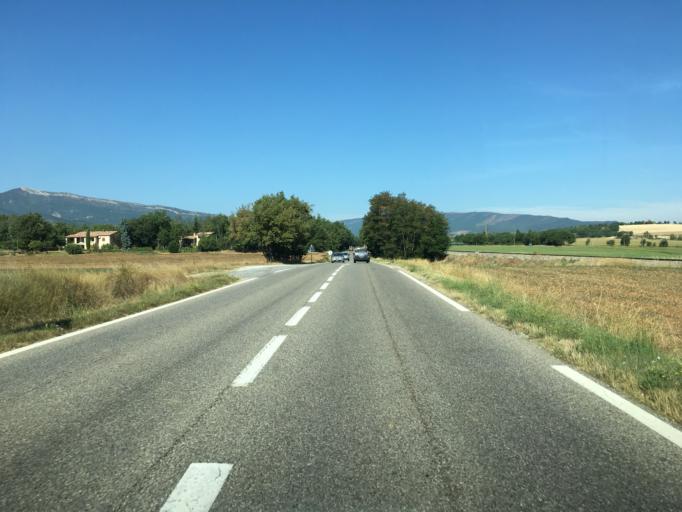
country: FR
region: Provence-Alpes-Cote d'Azur
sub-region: Departement des Alpes-de-Haute-Provence
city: Sisteron
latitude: 44.2512
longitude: 5.8827
